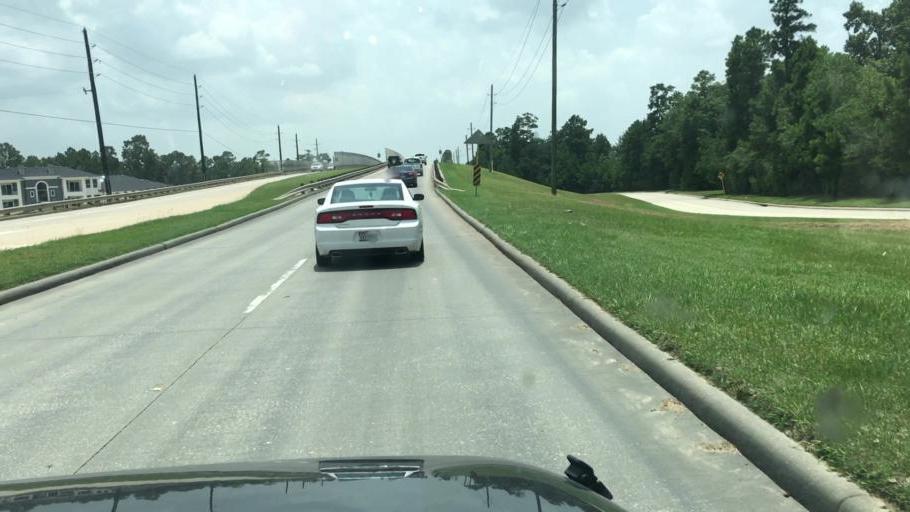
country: US
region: Texas
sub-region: Harris County
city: Atascocita
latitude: 29.9697
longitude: -95.1709
